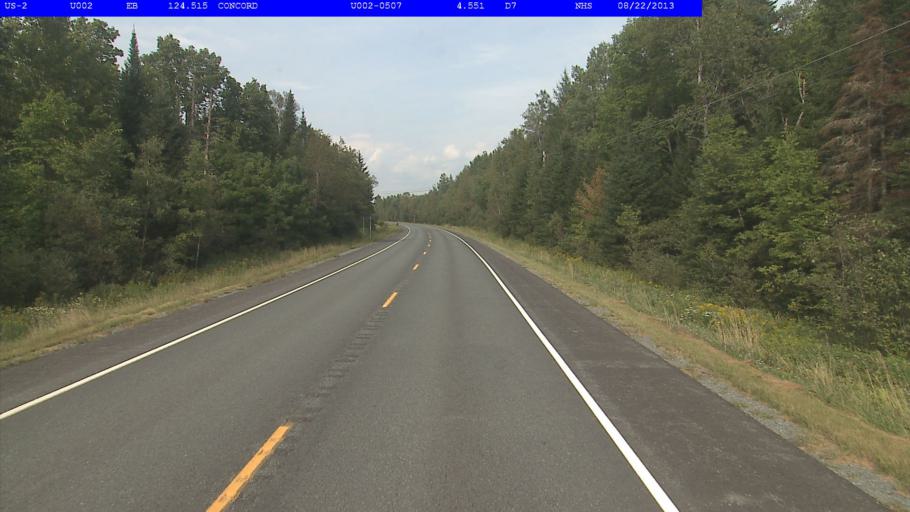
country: US
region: Vermont
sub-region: Caledonia County
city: St Johnsbury
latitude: 44.4576
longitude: -71.8660
